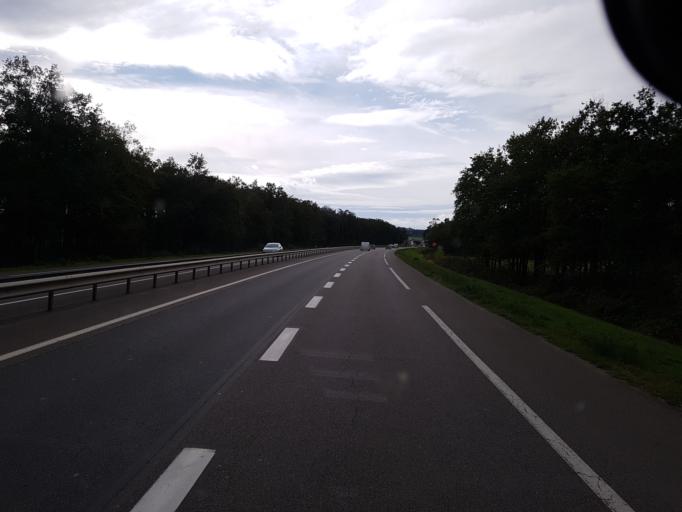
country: FR
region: Rhone-Alpes
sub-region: Departement de la Loire
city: Saint-Bonnet-les-Oules
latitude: 45.5331
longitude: 4.3048
